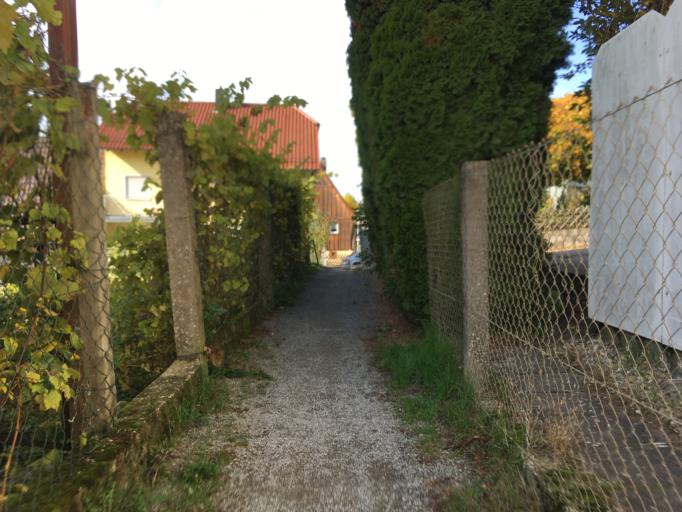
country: DE
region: Baden-Wuerttemberg
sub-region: Regierungsbezirk Stuttgart
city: Siegelsbach
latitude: 49.2552
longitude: 9.0434
